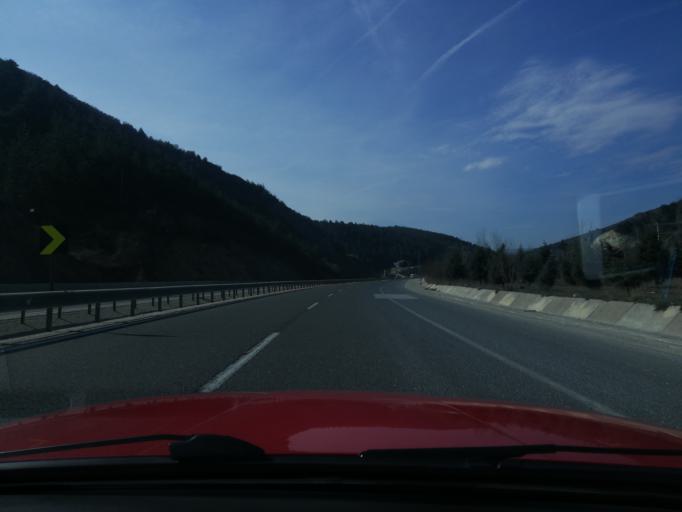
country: TR
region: Bilecik
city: Kuplu
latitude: 40.0212
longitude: 30.0269
